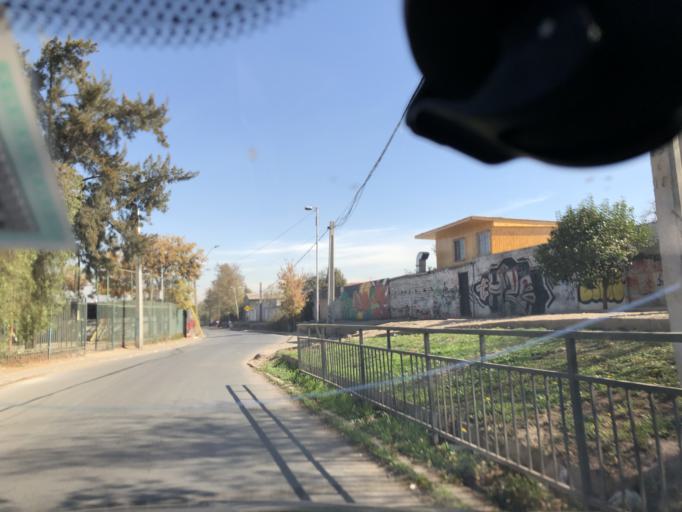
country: CL
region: Santiago Metropolitan
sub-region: Provincia de Santiago
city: La Pintana
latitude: -33.5862
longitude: -70.6037
